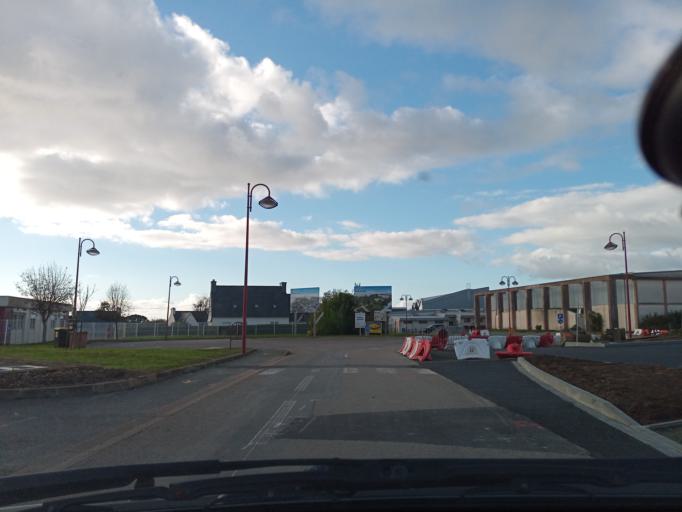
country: FR
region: Brittany
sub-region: Departement du Finistere
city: Plouhinec
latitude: 48.0165
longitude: -4.4910
